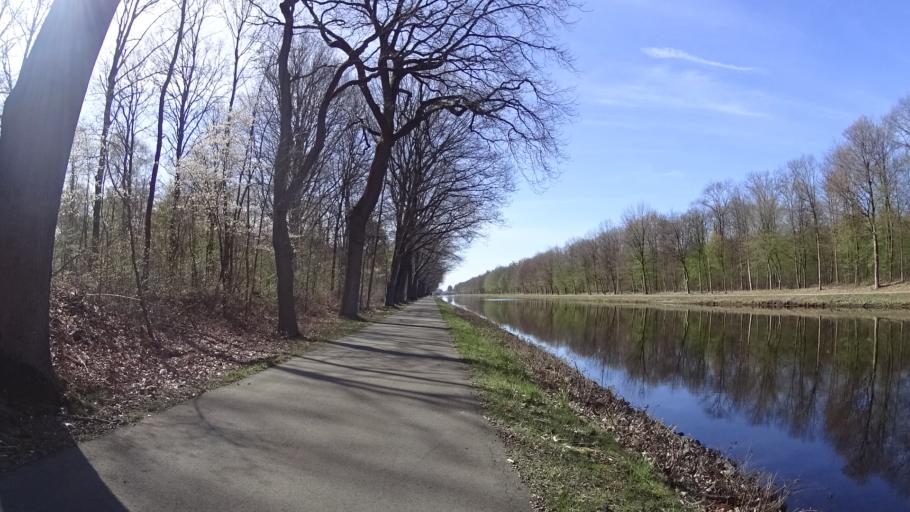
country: DE
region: Lower Saxony
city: Meppen
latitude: 52.6385
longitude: 7.3070
